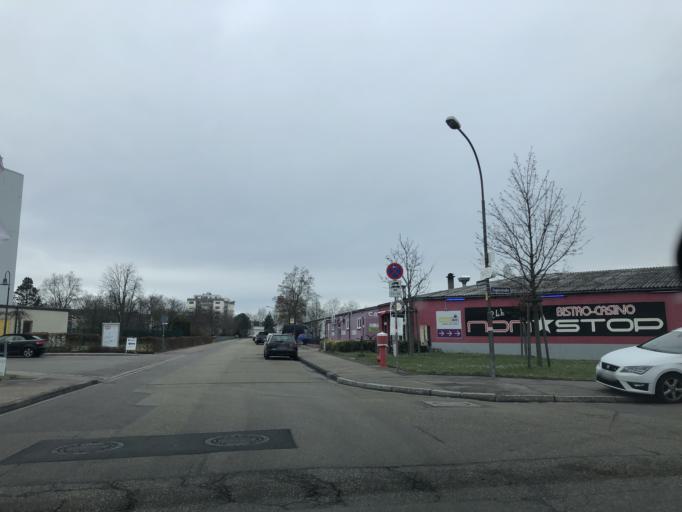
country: DE
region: Baden-Wuerttemberg
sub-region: Karlsruhe Region
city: Ettlingen
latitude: 48.9460
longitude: 8.3766
